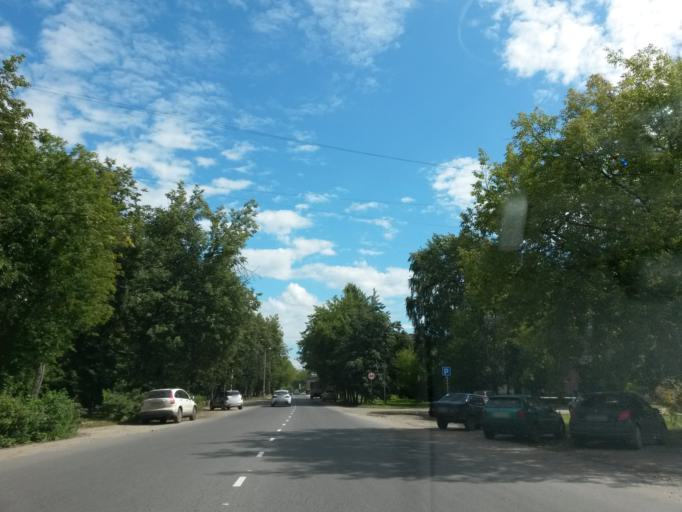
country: RU
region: Ivanovo
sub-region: Gorod Ivanovo
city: Ivanovo
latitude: 56.9904
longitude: 40.9721
